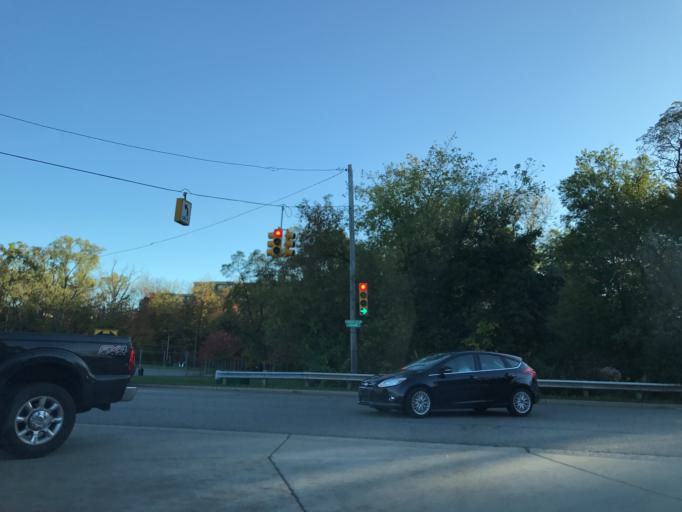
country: US
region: Michigan
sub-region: Oakland County
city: Farmington
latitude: 42.4663
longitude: -83.3715
